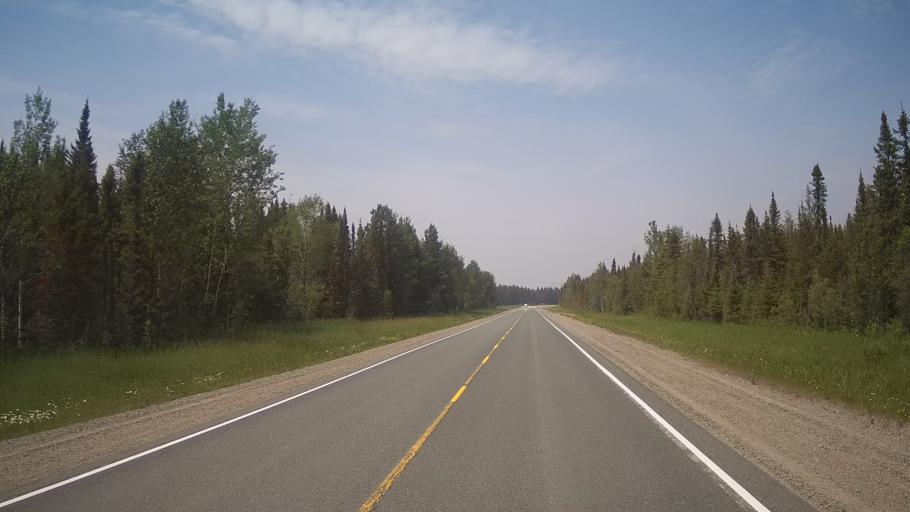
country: CA
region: Ontario
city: Timmins
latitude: 48.7258
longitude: -81.3486
